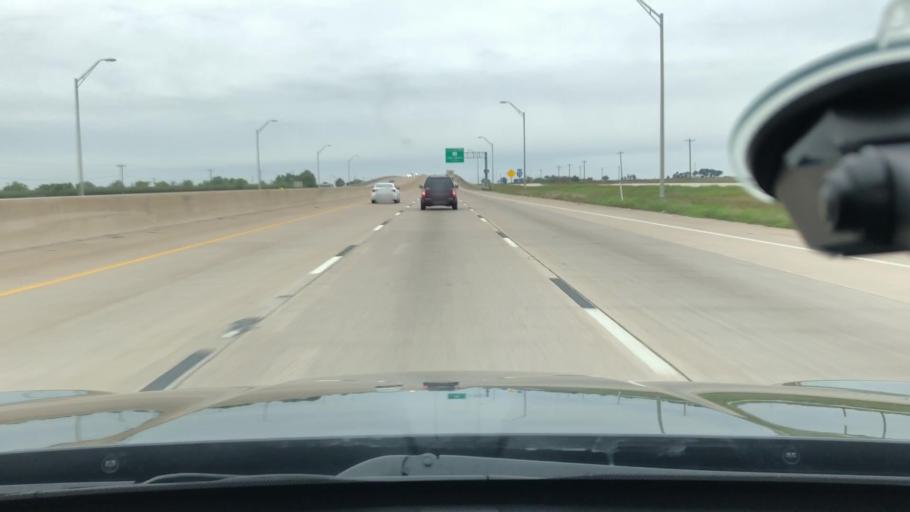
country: US
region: Texas
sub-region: Hill County
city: Hillsboro
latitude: 31.9337
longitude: -97.1050
